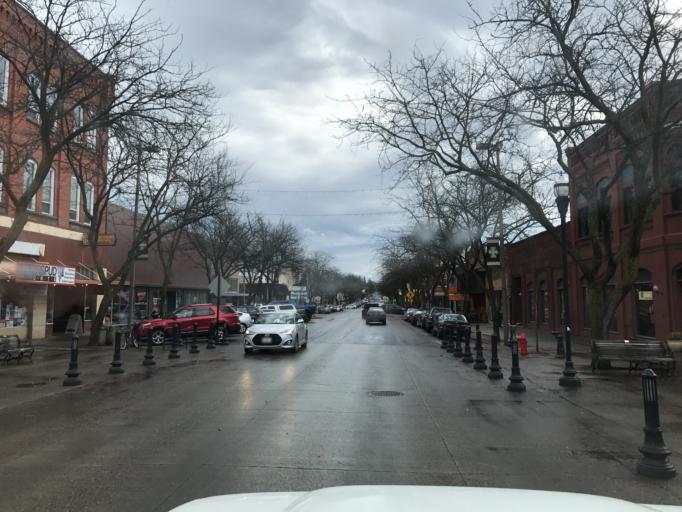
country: US
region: Idaho
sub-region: Latah County
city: Moscow
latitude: 46.7318
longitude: -117.0014
